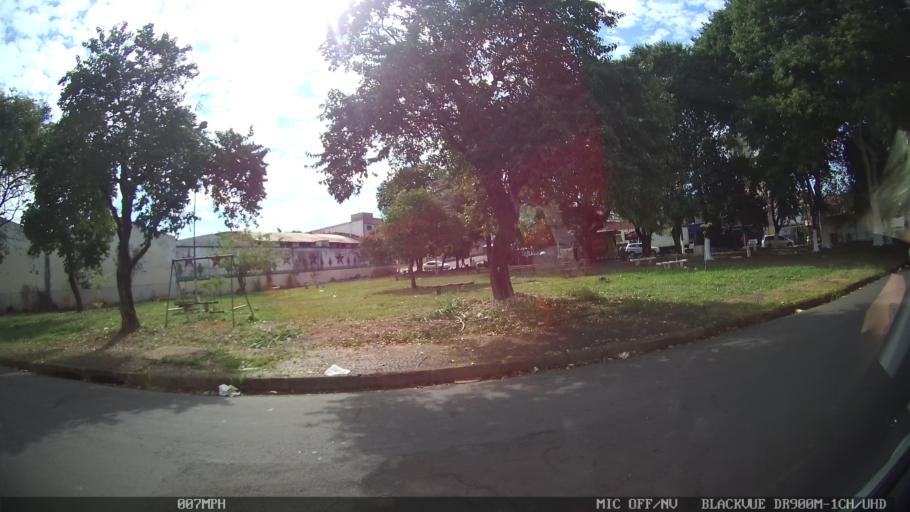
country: BR
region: Sao Paulo
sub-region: Santa Barbara D'Oeste
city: Santa Barbara d'Oeste
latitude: -22.7490
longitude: -47.4225
